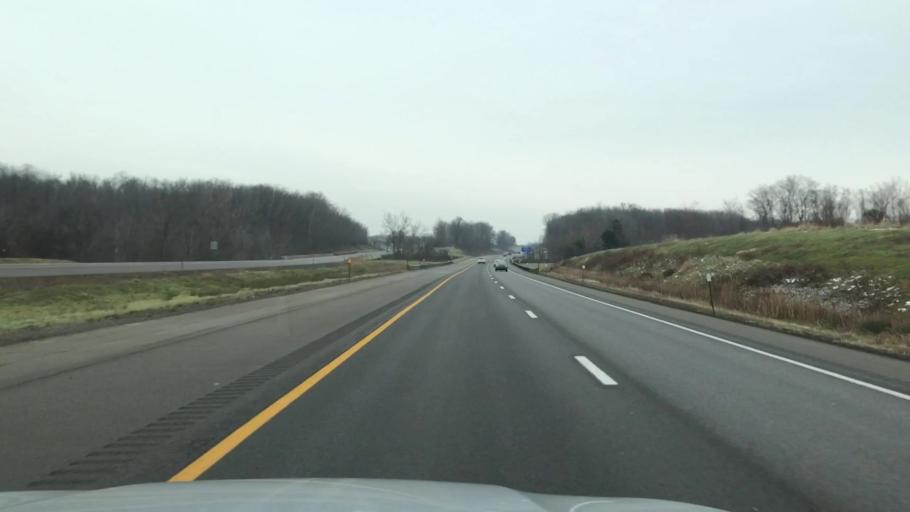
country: US
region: New York
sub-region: Erie County
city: Angola
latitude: 42.6296
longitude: -78.9966
